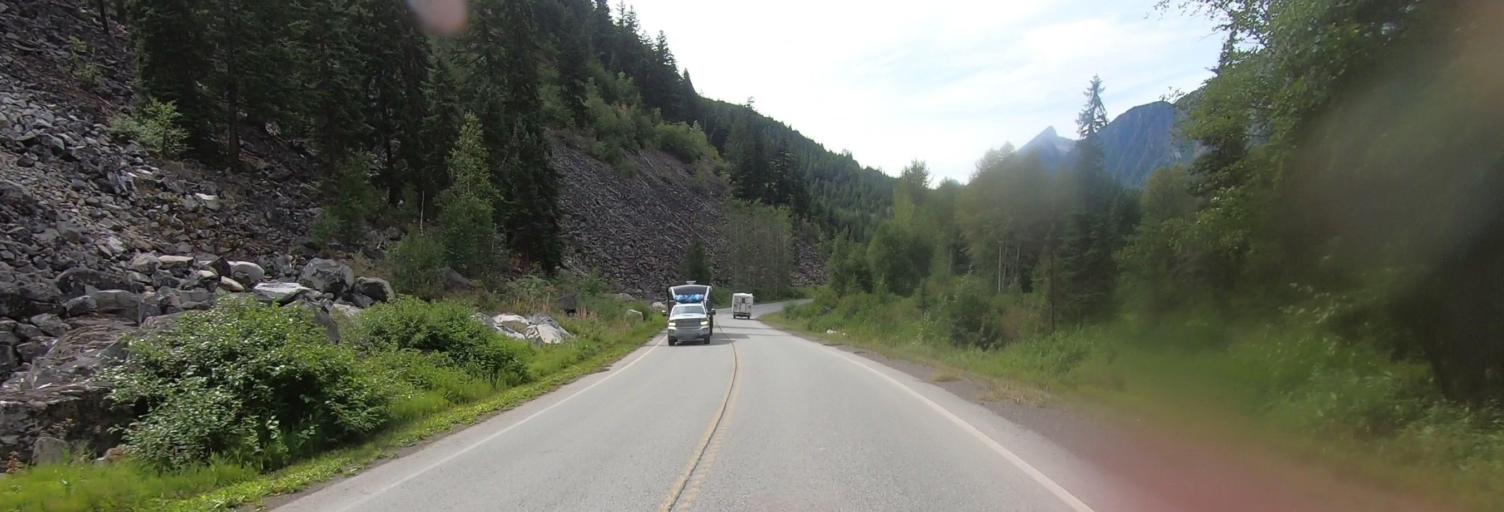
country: CA
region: British Columbia
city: Lillooet
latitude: 50.5399
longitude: -122.1149
